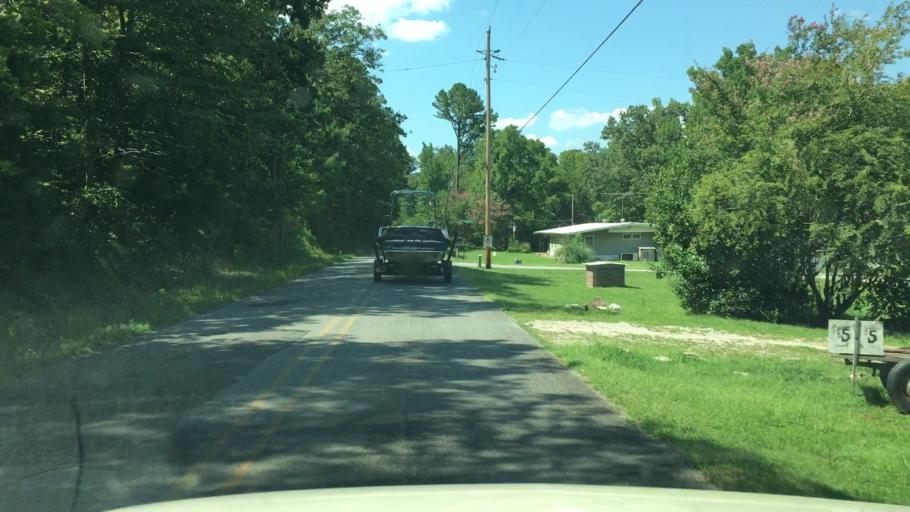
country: US
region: Arkansas
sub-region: Garland County
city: Piney
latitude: 34.5285
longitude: -93.3358
